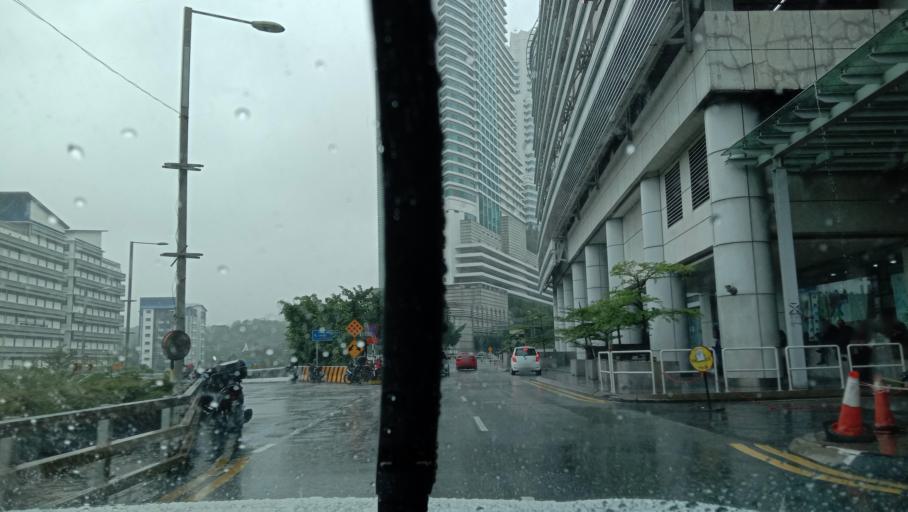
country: MY
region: Kuala Lumpur
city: Kuala Lumpur
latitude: 3.1335
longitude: 101.6841
